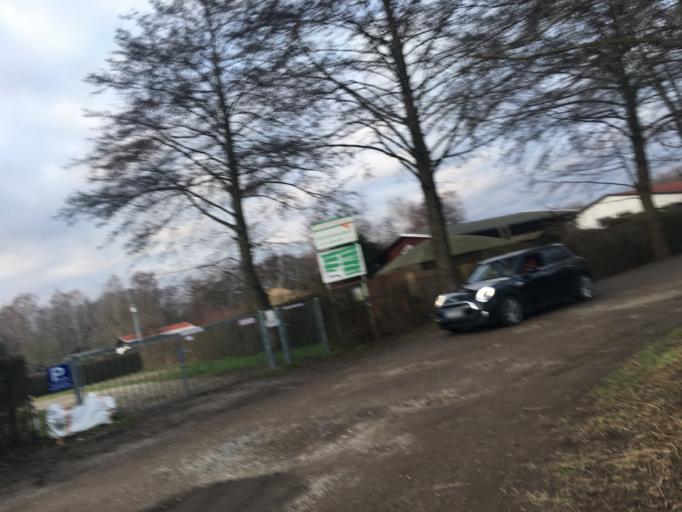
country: DE
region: Berlin
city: Karow
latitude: 52.6184
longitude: 13.4687
